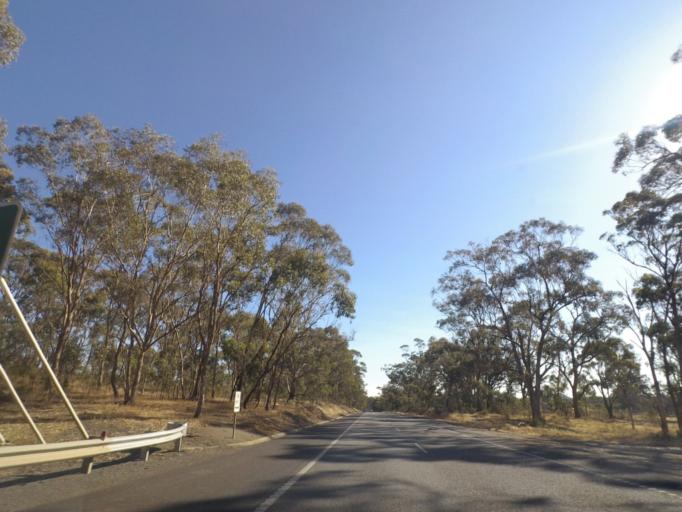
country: AU
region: Victoria
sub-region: Murrindindi
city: Kinglake West
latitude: -37.1740
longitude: 145.0739
